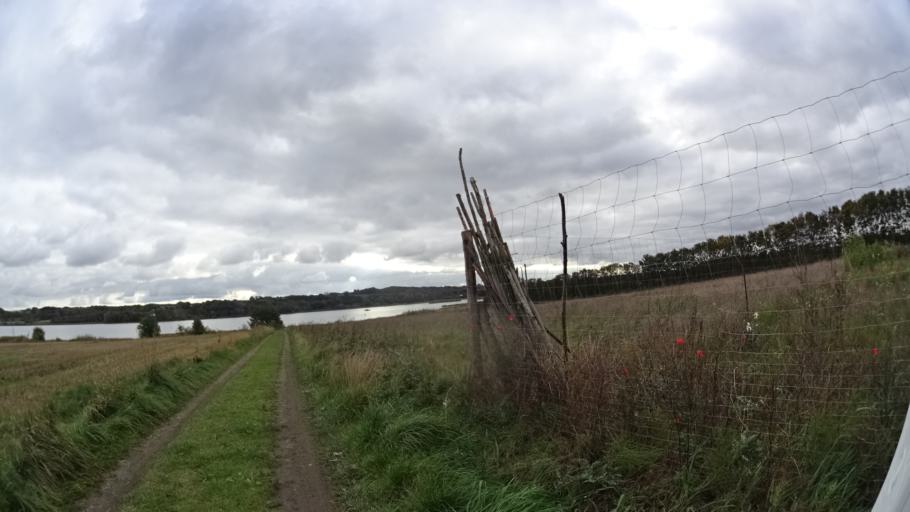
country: DK
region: Central Jutland
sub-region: Arhus Kommune
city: Kolt
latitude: 56.1479
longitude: 10.0699
